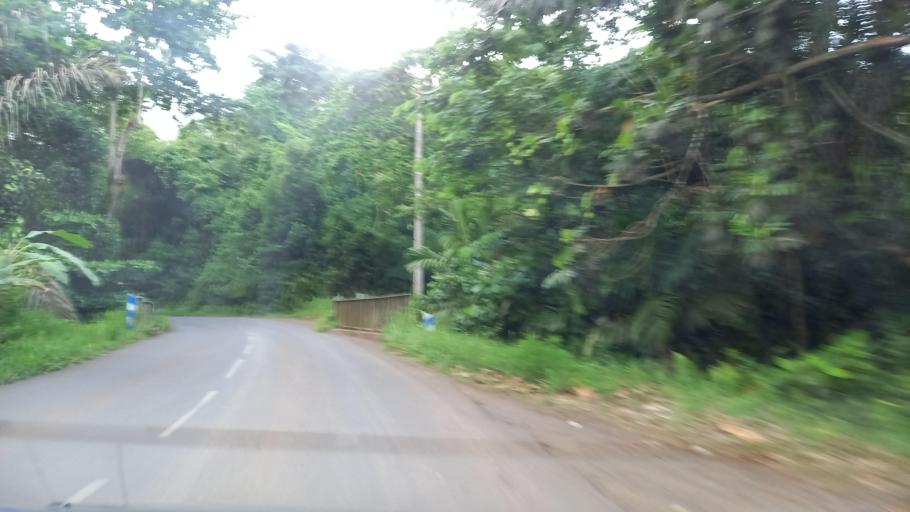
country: YT
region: M'Tsangamouji
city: M'Tsangamouji
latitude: -12.7611
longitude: 45.1032
